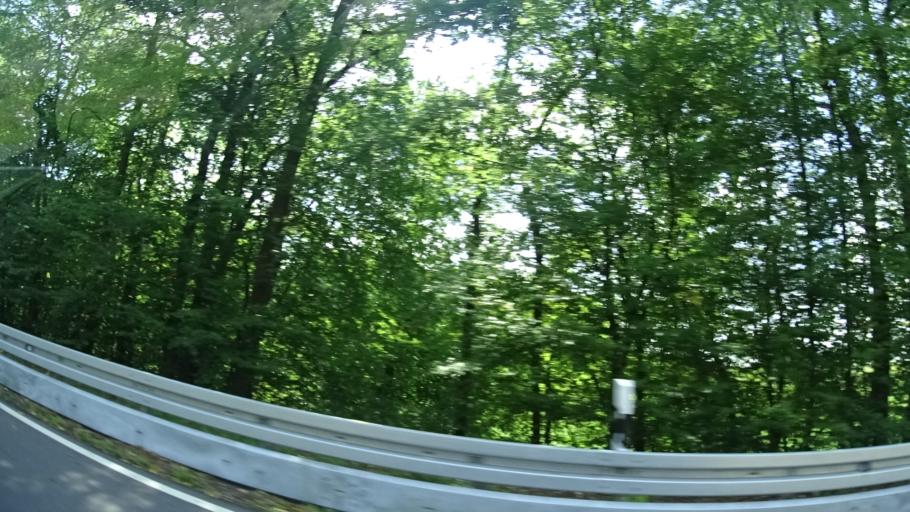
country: DE
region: Bavaria
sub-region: Regierungsbezirk Unterfranken
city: Kirchlauter
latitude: 50.0192
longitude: 10.7323
